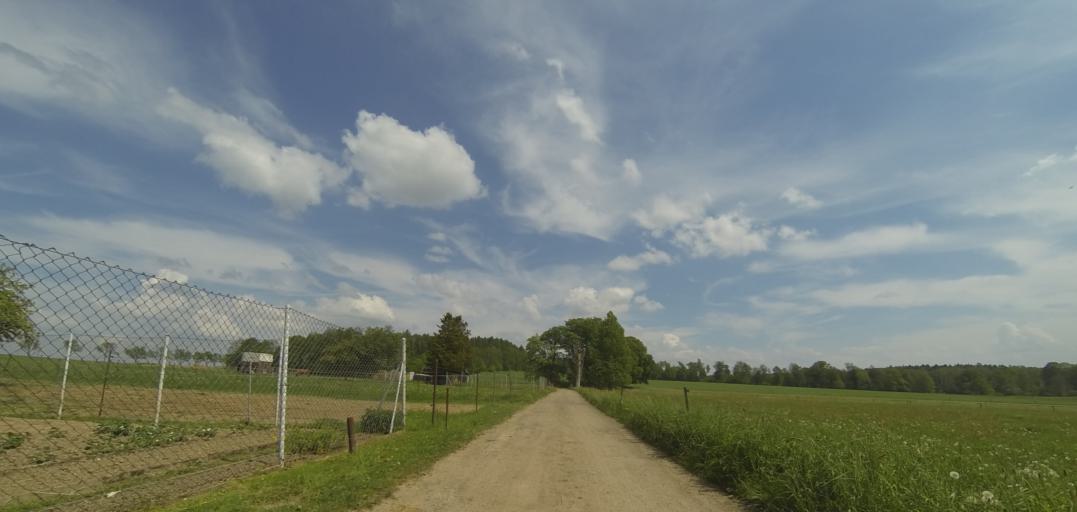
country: DE
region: Saxony
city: Grossharthau
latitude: 51.1075
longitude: 14.1130
